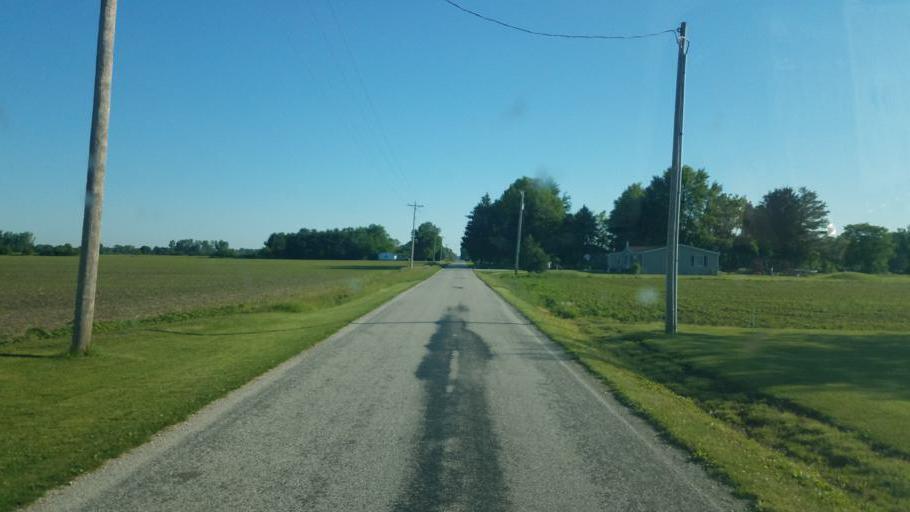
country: US
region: Ohio
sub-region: Marion County
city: Marion
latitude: 40.6202
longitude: -82.9909
